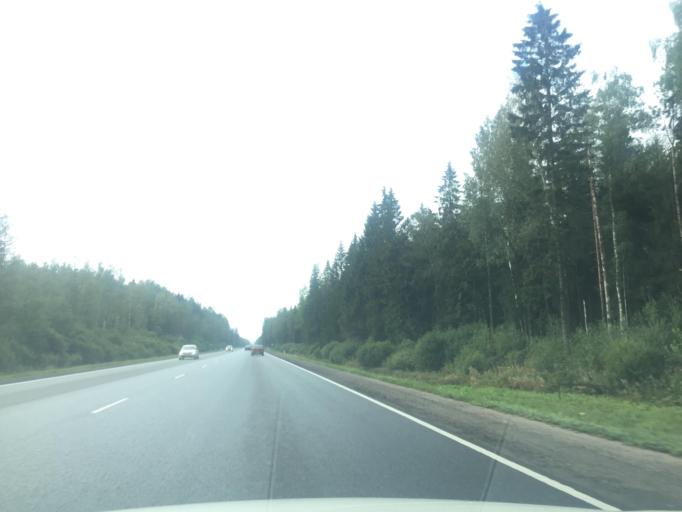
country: RU
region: Leningrad
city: Rozhdestveno
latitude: 59.4144
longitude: 29.9770
